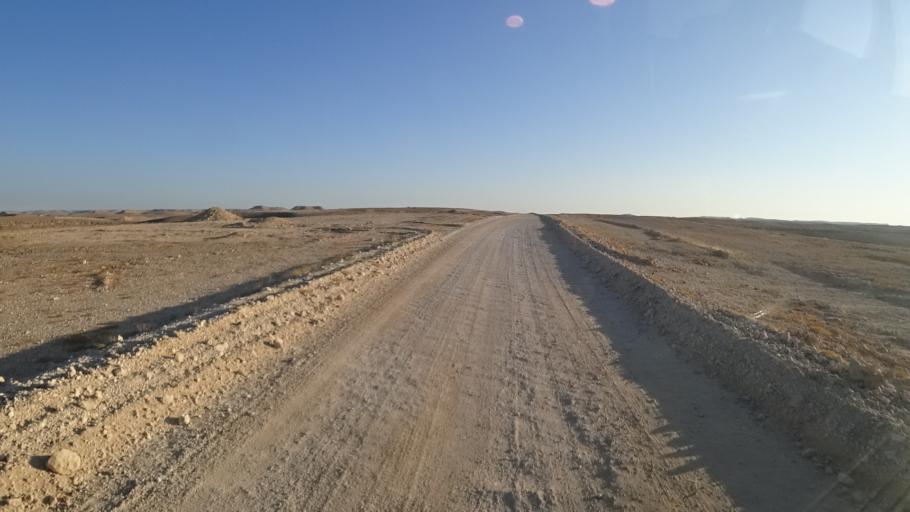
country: YE
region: Al Mahrah
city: Hawf
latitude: 17.1681
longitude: 53.3522
